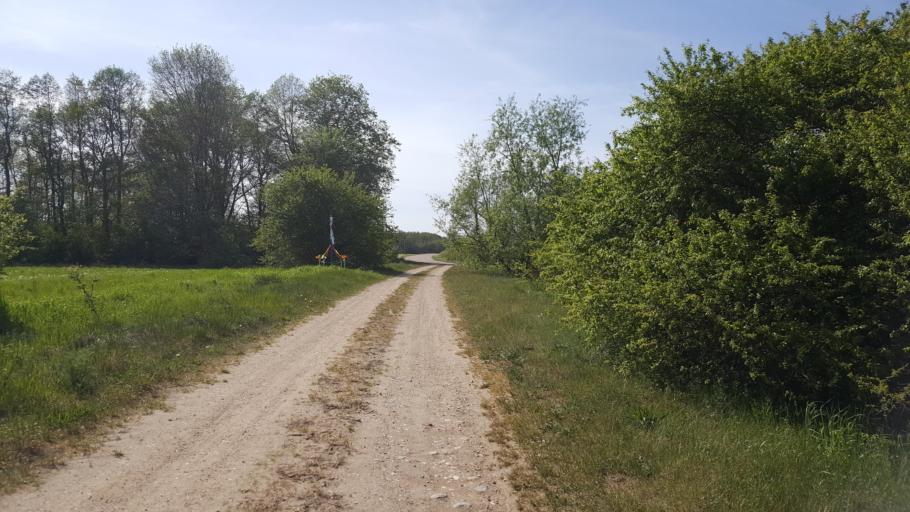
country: BY
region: Brest
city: Zhabinka
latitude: 52.3125
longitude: 24.0377
